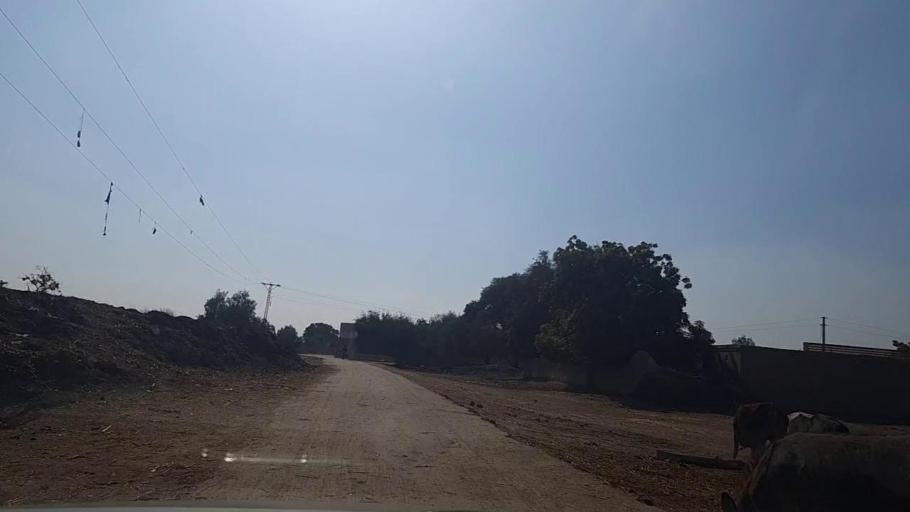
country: PK
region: Sindh
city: Sehwan
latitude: 26.2738
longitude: 68.0357
